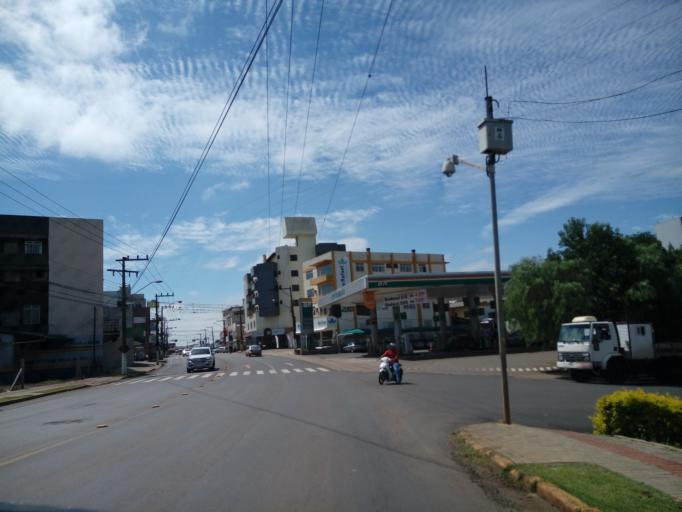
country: BR
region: Santa Catarina
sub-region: Chapeco
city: Chapeco
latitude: -27.0953
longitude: -52.6276
